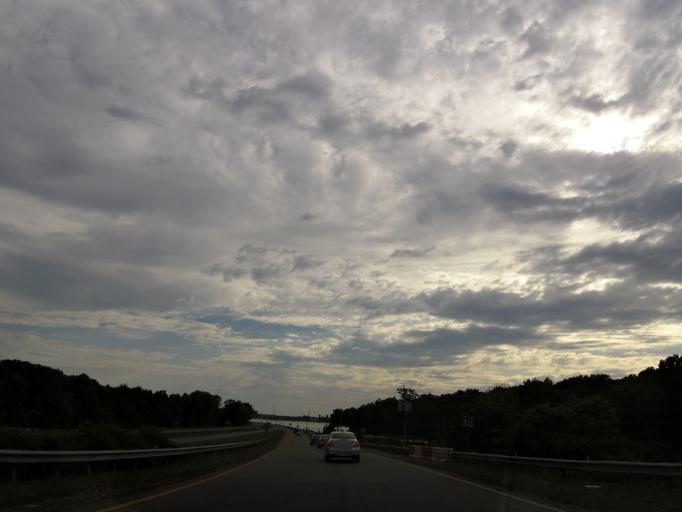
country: US
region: Alabama
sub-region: Morgan County
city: Decatur
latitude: 34.6293
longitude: -86.9529
